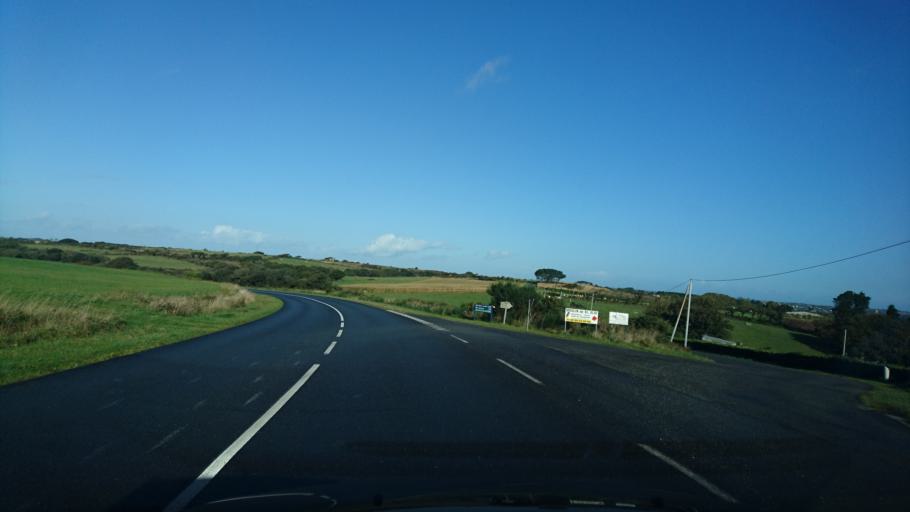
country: FR
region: Brittany
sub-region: Departement du Finistere
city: Plouarzel
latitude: 48.4373
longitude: -4.7162
